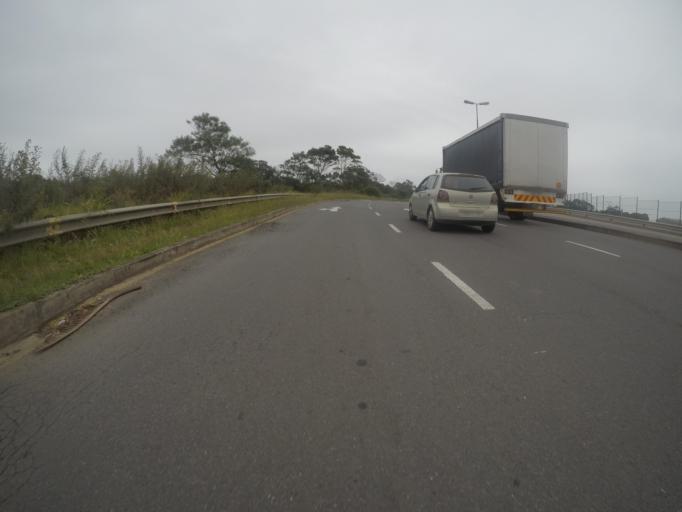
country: ZA
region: Eastern Cape
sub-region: Buffalo City Metropolitan Municipality
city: East London
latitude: -32.9705
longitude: 27.8957
